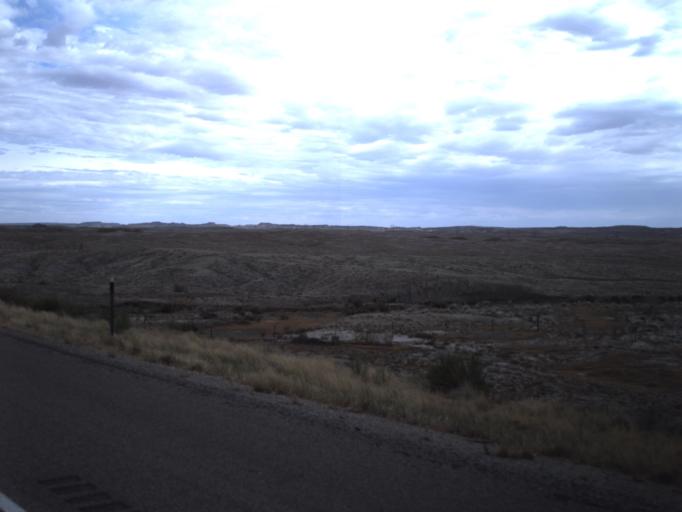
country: US
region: Utah
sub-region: Grand County
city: Moab
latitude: 38.9445
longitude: -110.0391
